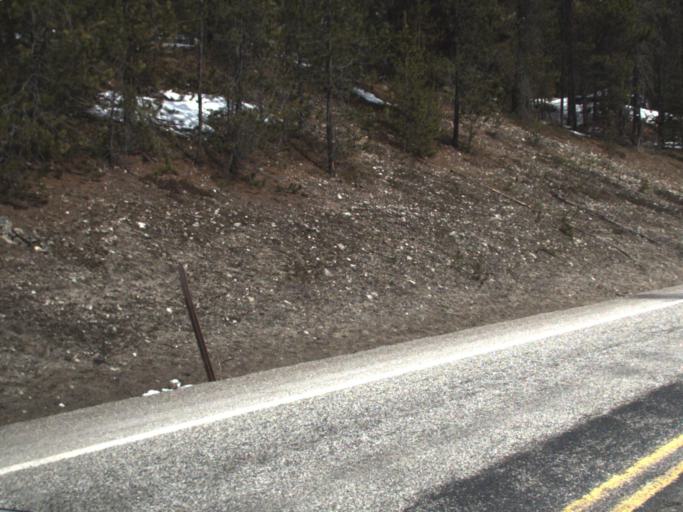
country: US
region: Washington
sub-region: Stevens County
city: Colville
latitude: 48.6466
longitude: -117.5150
